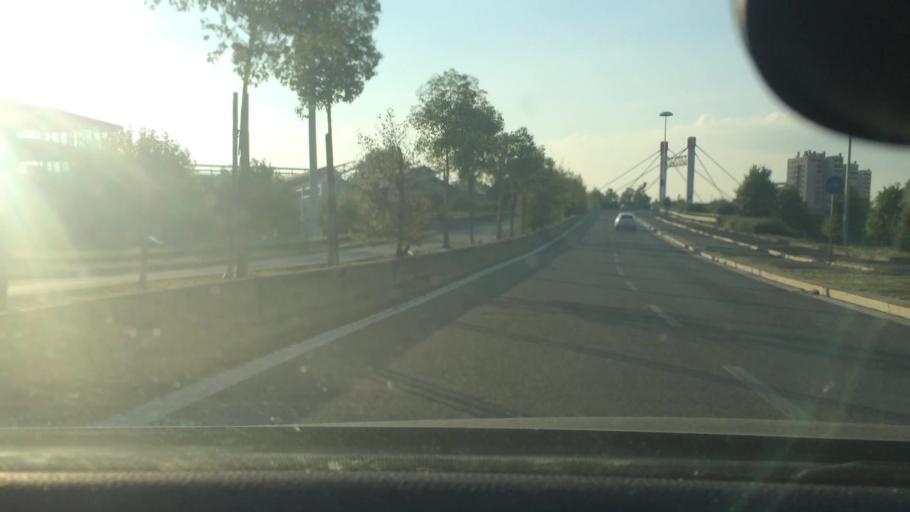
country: IT
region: Lombardy
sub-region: Citta metropolitana di Milano
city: Novate Milanese
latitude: 45.5033
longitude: 9.1420
